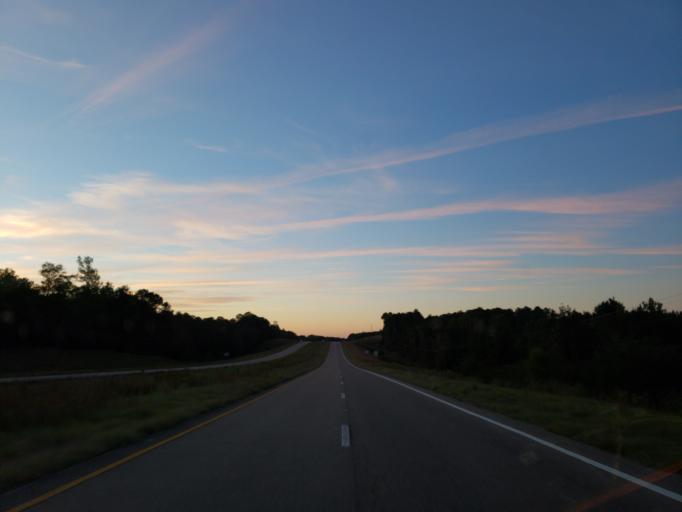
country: US
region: Mississippi
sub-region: Wayne County
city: Waynesboro
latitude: 31.7142
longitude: -88.6317
